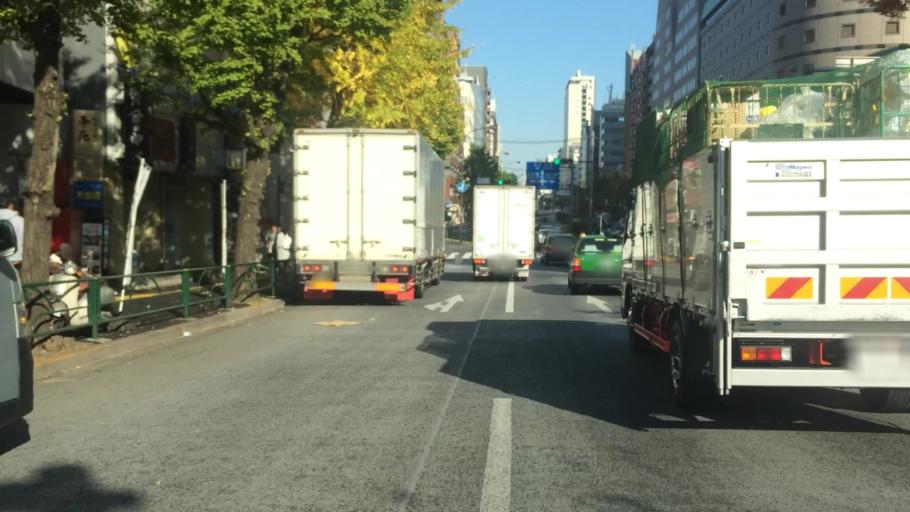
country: JP
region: Tokyo
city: Tokyo
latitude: 35.6943
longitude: 139.7067
